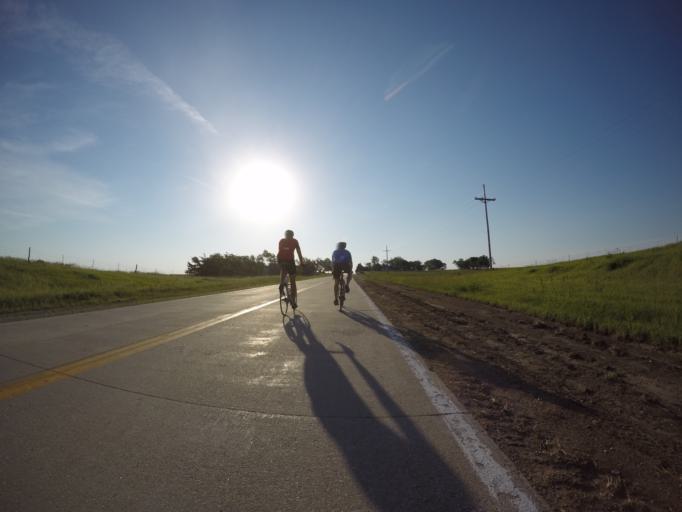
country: US
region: Nebraska
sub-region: Gage County
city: Wymore
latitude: 40.0448
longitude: -96.6209
